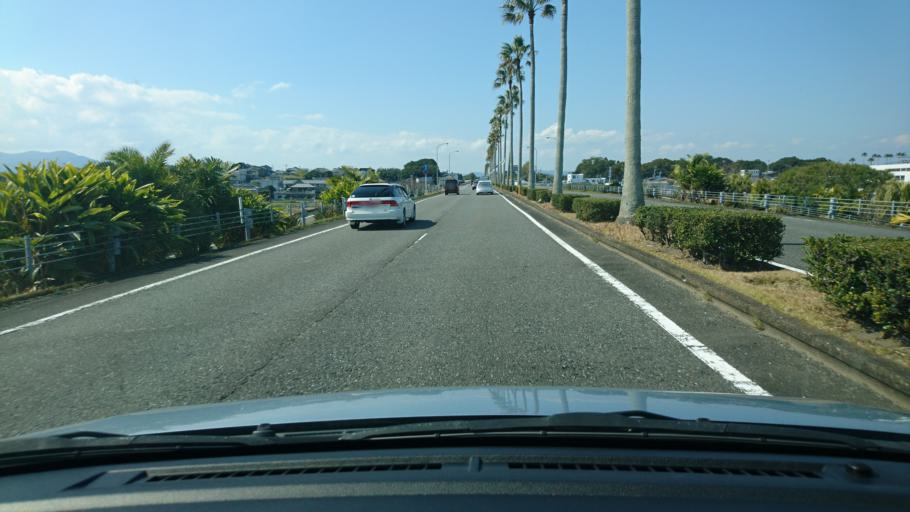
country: JP
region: Miyazaki
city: Miyazaki-shi
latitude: 31.8669
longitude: 131.4356
